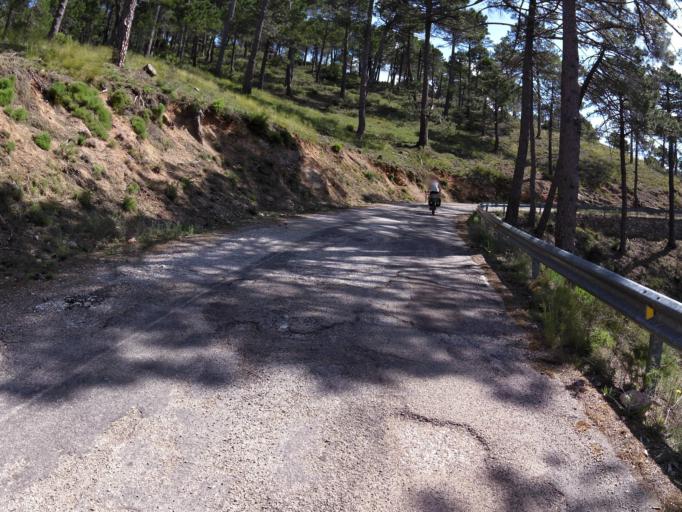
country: ES
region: Castille-La Mancha
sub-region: Provincia de Albacete
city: Riopar
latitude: 38.5235
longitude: -2.4342
